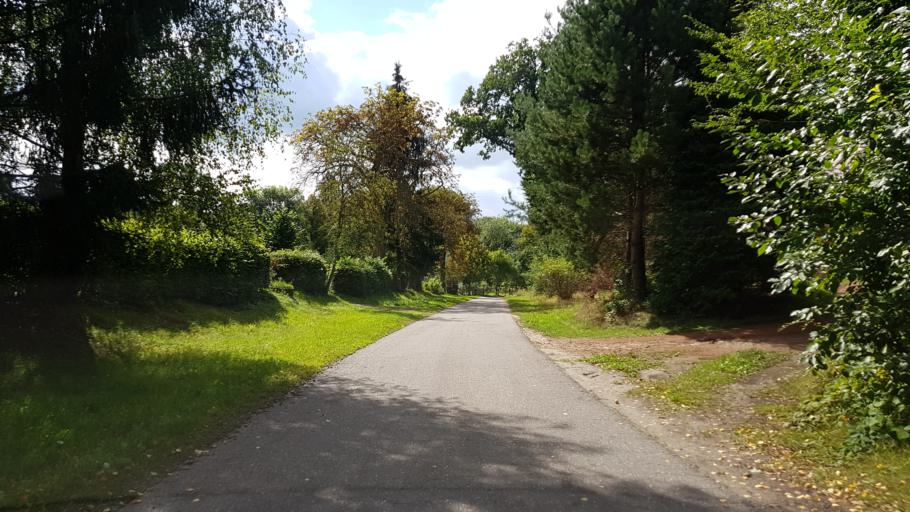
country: PL
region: West Pomeranian Voivodeship
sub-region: Powiat bialogardzki
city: Tychowo
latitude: 53.9927
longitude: 16.3053
